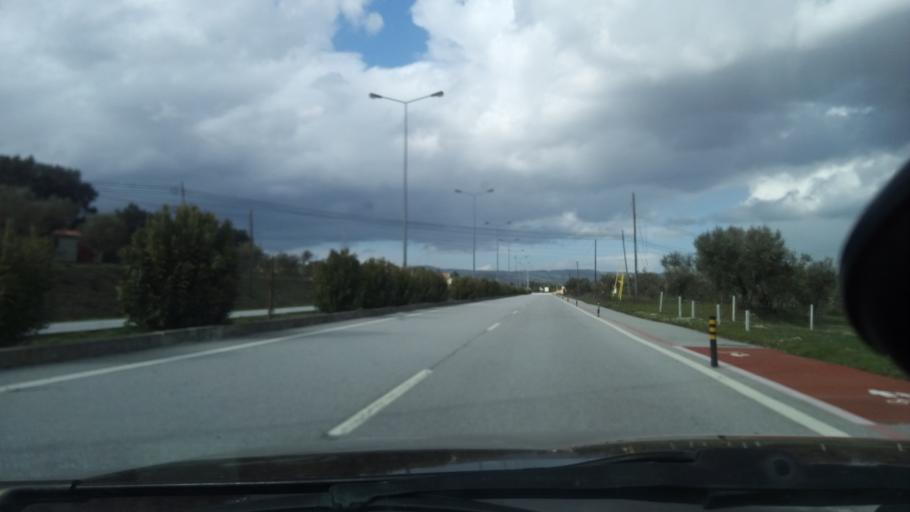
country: PT
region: Guarda
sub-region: Celorico da Beira
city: Celorico da Beira
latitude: 40.6377
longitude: -7.3840
